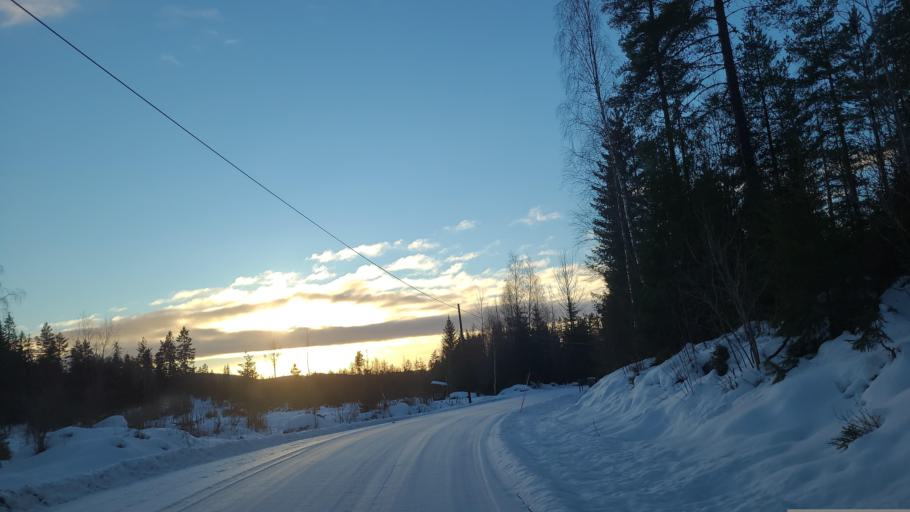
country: SE
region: Gaevleborg
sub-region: Bollnas Kommun
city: Kilafors
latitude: 61.3742
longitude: 16.6815
